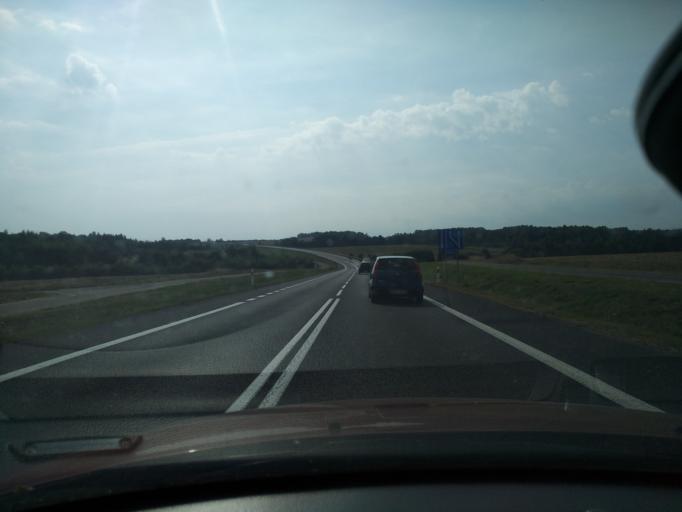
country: PL
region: Lower Silesian Voivodeship
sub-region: Powiat lwowecki
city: Gryfow Slaski
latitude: 51.0050
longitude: 15.4516
